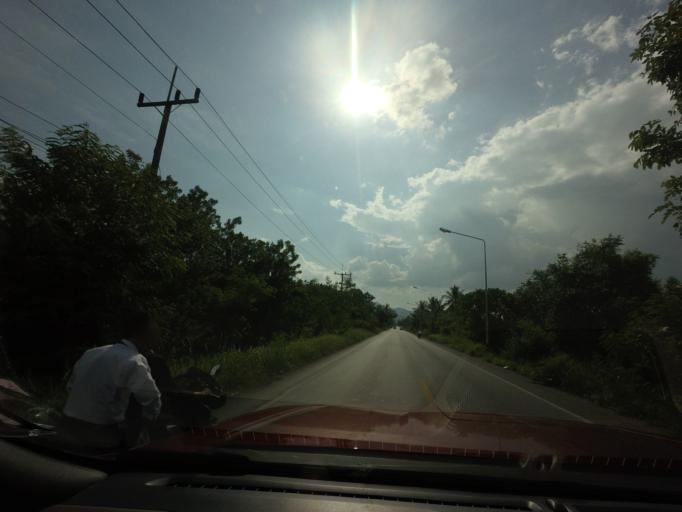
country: TH
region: Yala
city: Yala
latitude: 6.5652
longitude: 101.2118
